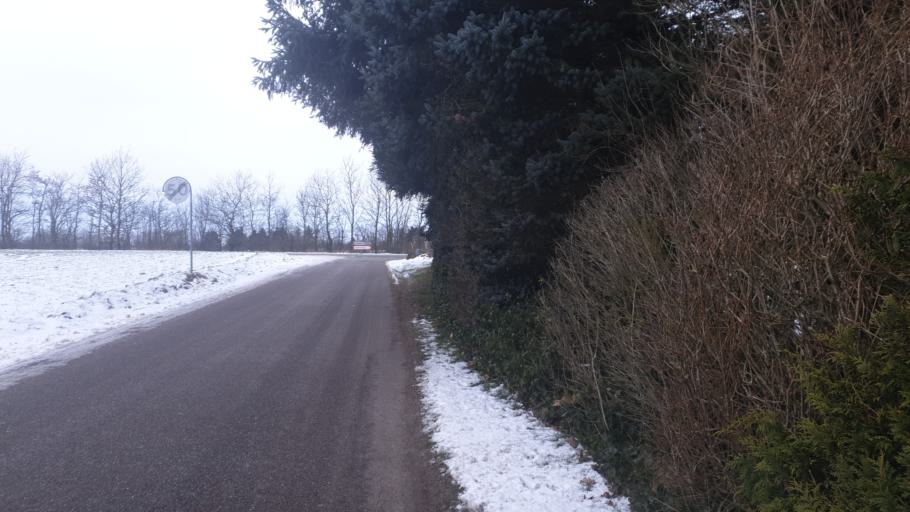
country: DK
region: Central Jutland
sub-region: Hedensted Kommune
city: Hedensted
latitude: 55.7926
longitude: 9.7056
